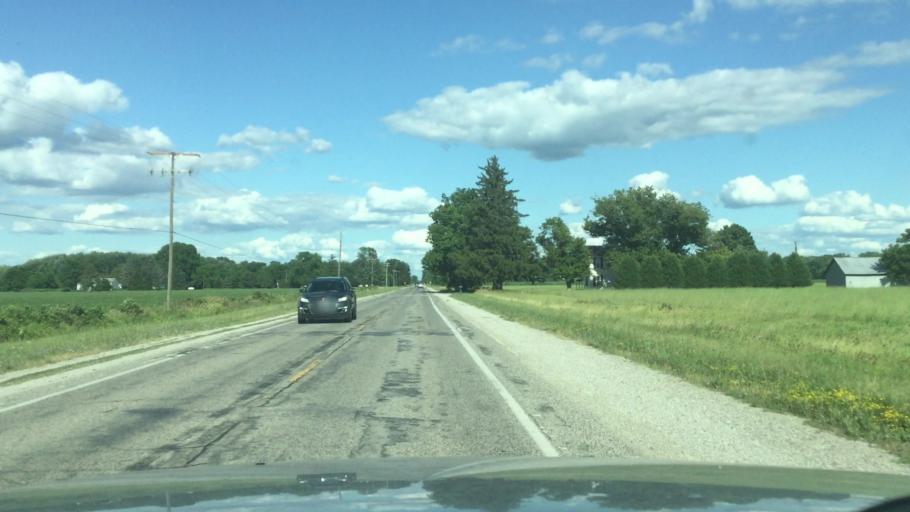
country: US
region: Michigan
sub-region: Saginaw County
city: Shields
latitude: 43.3798
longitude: -84.1102
